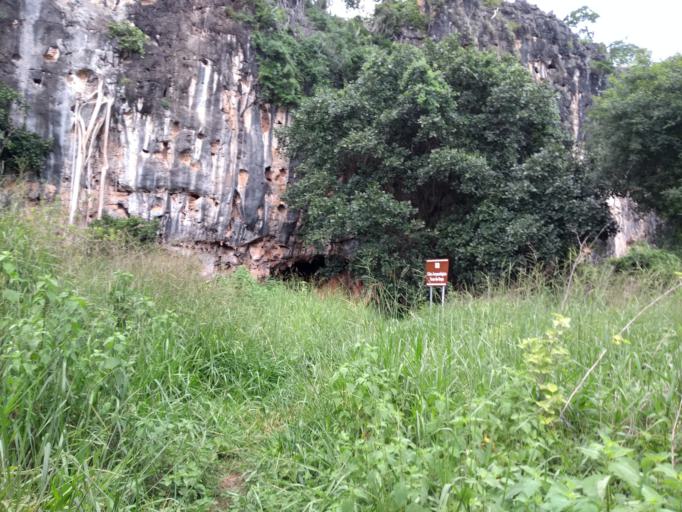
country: BR
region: Goias
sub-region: Formosa
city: Formosa
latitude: -15.4932
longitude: -47.3024
